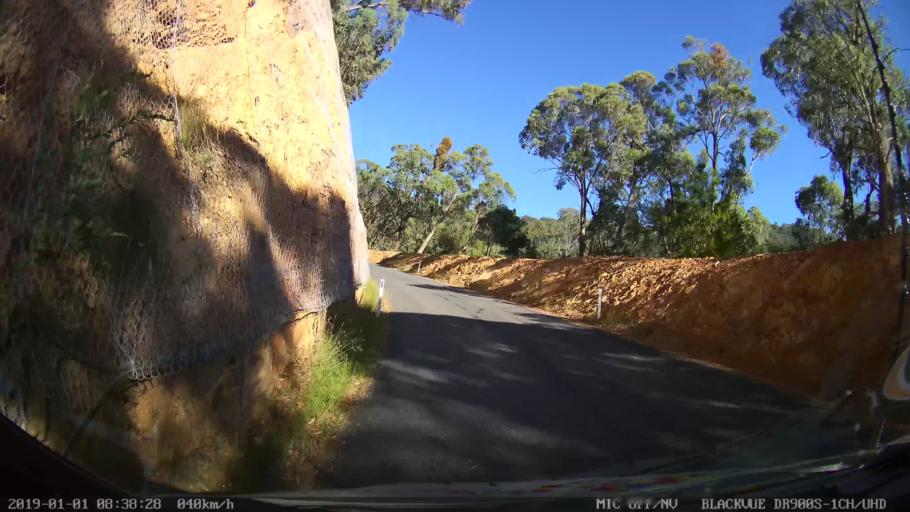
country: AU
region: New South Wales
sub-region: Snowy River
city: Jindabyne
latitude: -36.3320
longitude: 148.1978
